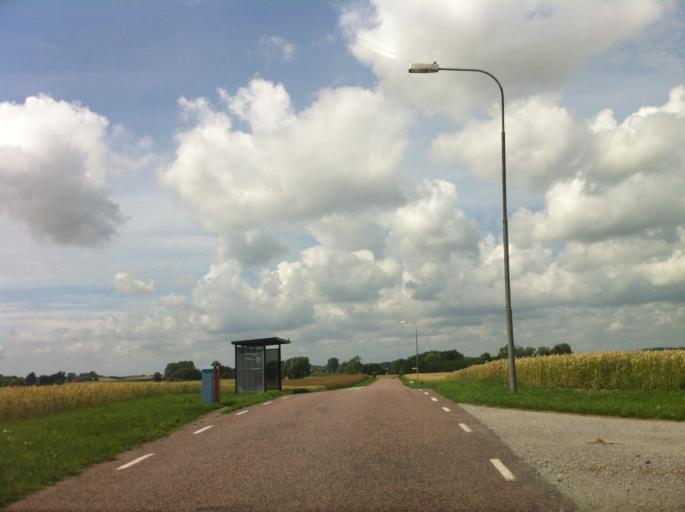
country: SE
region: Skane
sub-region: Skurups Kommun
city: Skurup
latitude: 55.4208
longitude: 13.4501
